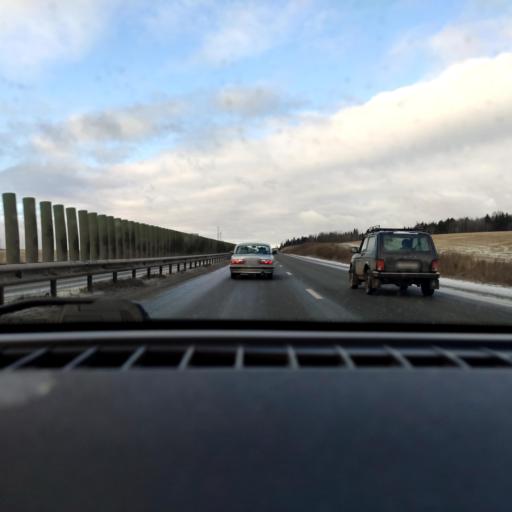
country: RU
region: Perm
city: Froly
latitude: 57.9349
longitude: 56.2327
